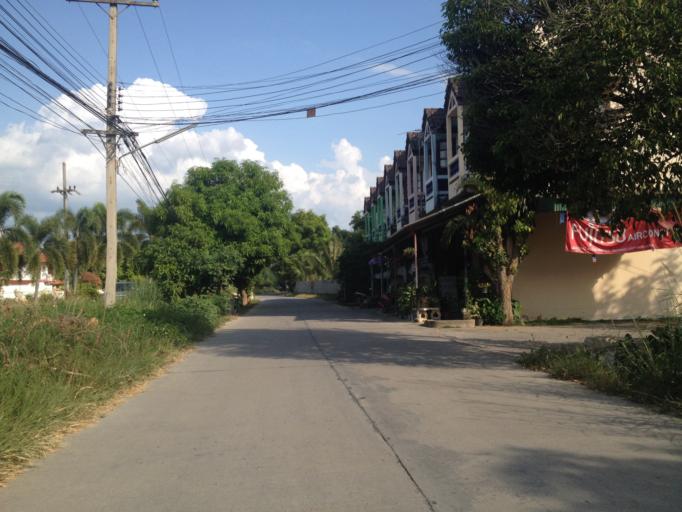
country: TH
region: Chiang Mai
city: Hang Dong
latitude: 18.7040
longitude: 98.9267
